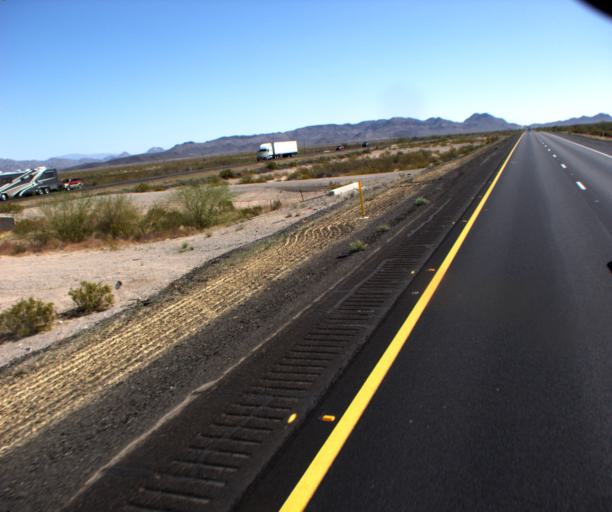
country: US
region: Arizona
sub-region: La Paz County
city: Salome
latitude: 33.6238
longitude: -113.7207
